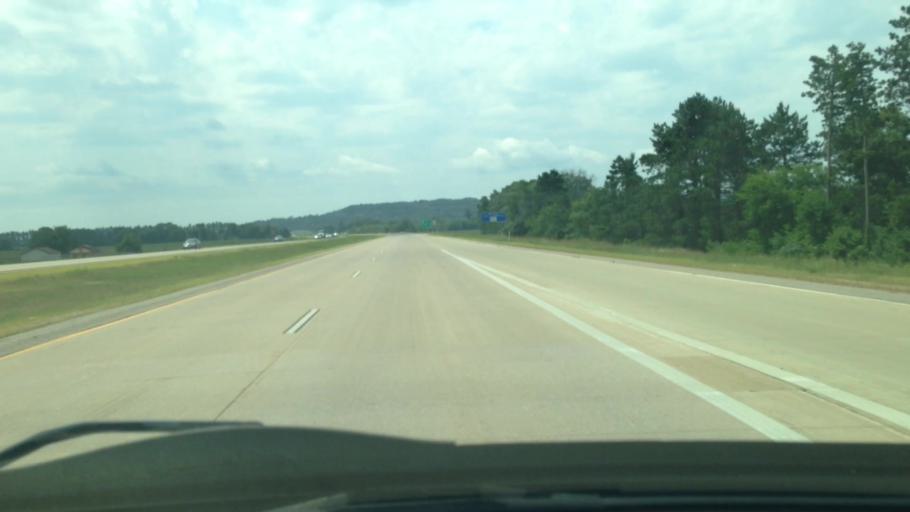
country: US
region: Wisconsin
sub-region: Sauk County
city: West Baraboo
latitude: 43.5284
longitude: -89.7880
